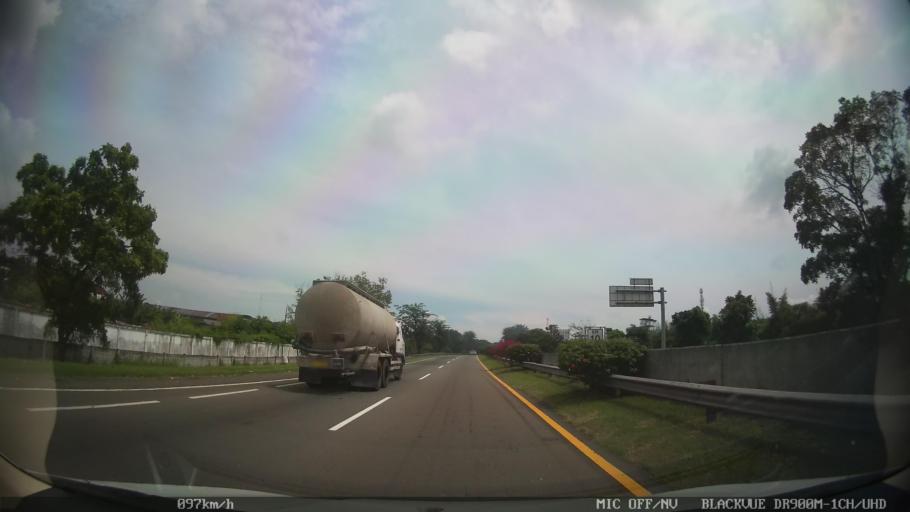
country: ID
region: North Sumatra
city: Labuhan Deli
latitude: 3.6756
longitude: 98.6802
